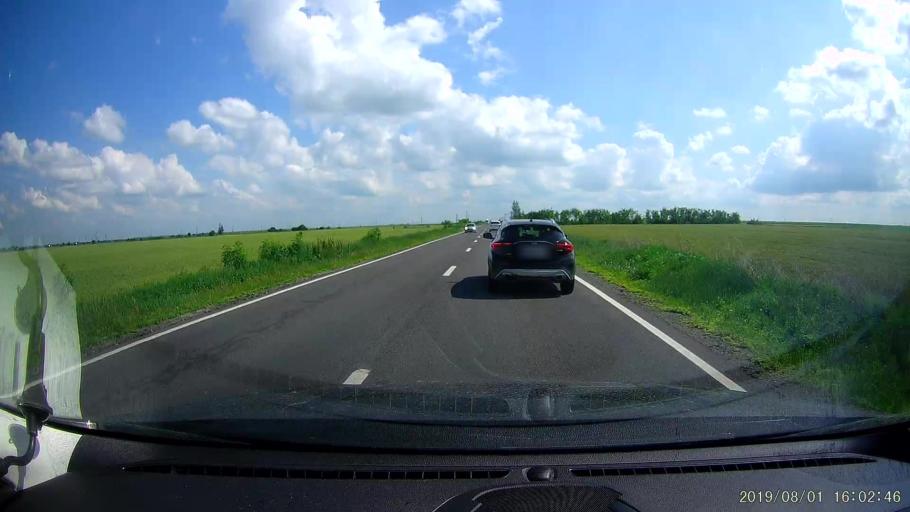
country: RO
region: Ialomita
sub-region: Comuna Ciulnita
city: Ciulnita
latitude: 44.4839
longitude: 27.3863
